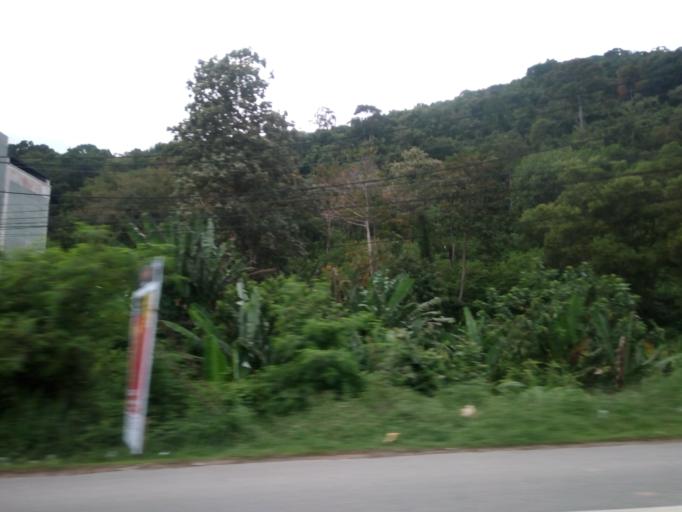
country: TH
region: Phuket
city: Ban Ko Kaeo
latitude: 7.9231
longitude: 98.3711
